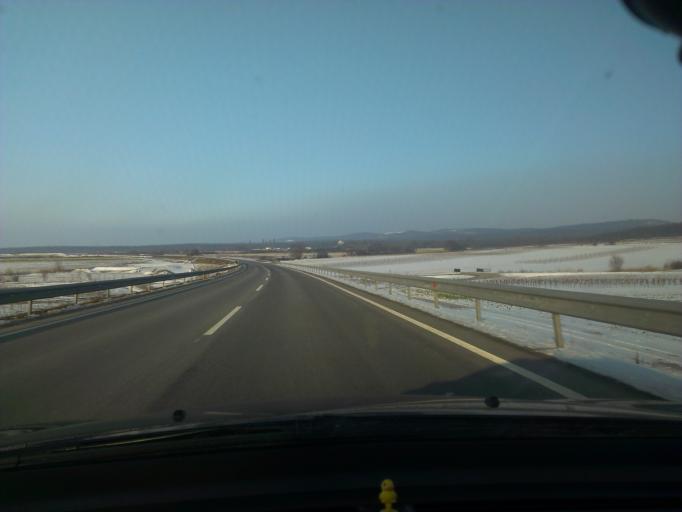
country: AT
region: Burgenland
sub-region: Eisenstadt-Umgebung
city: Schutzen am Gebirge
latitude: 47.8666
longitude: 16.6325
